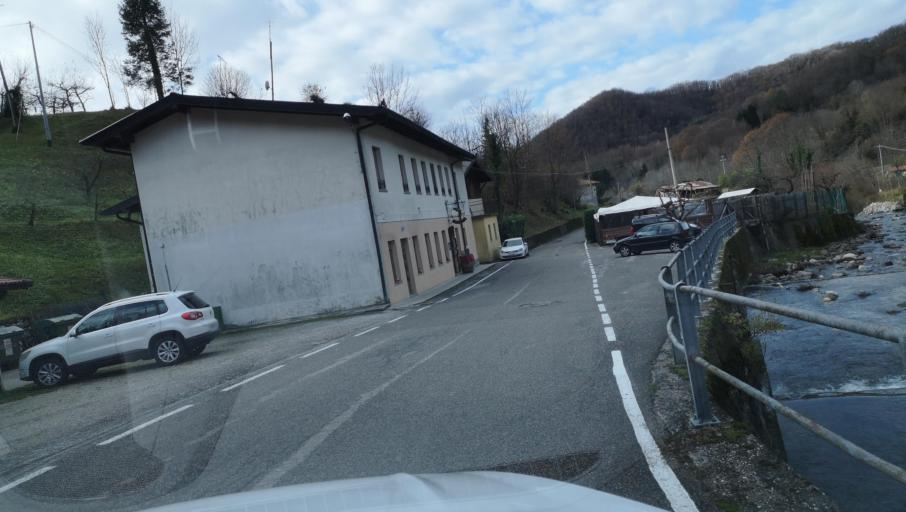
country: IT
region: Friuli Venezia Giulia
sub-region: Provincia di Udine
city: Attimis
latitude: 46.2170
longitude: 13.3209
